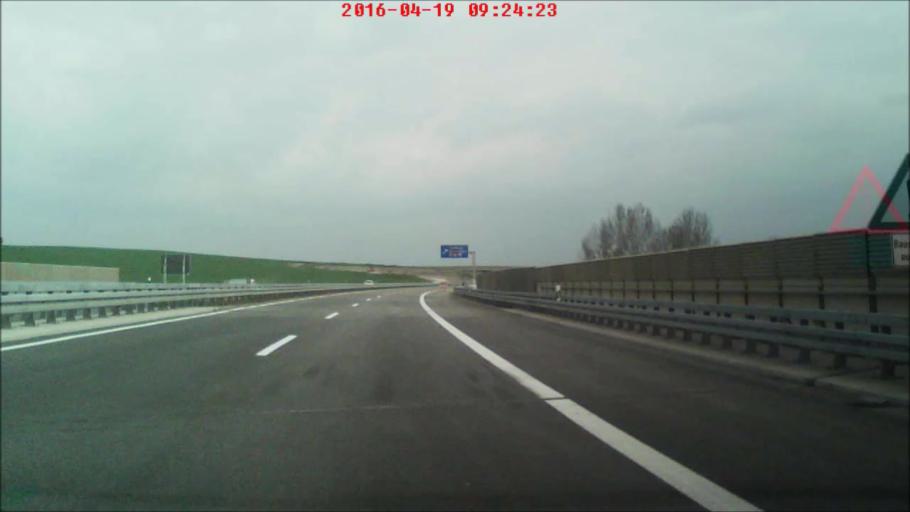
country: DE
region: Thuringia
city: Soemmerda
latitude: 51.1790
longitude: 11.1555
